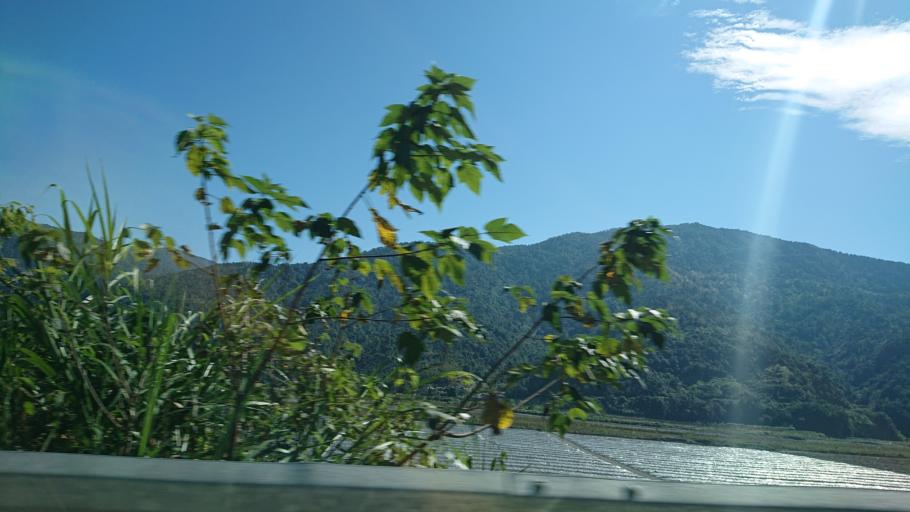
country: TW
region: Taiwan
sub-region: Yilan
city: Yilan
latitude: 24.5960
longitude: 121.5113
